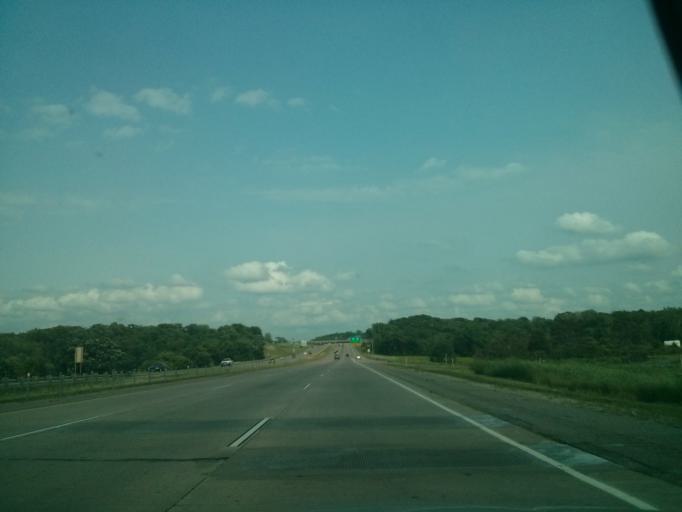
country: US
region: Wisconsin
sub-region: Saint Croix County
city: Hudson
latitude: 44.9637
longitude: -92.6940
